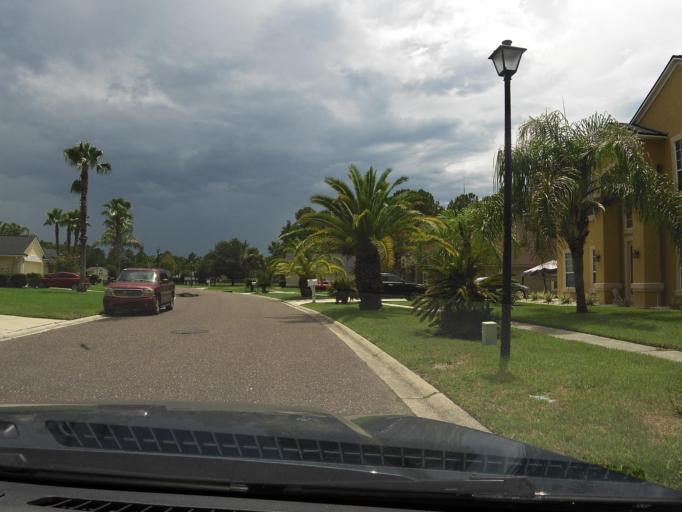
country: US
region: Florida
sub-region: Duval County
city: Jacksonville
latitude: 30.4253
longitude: -81.7254
